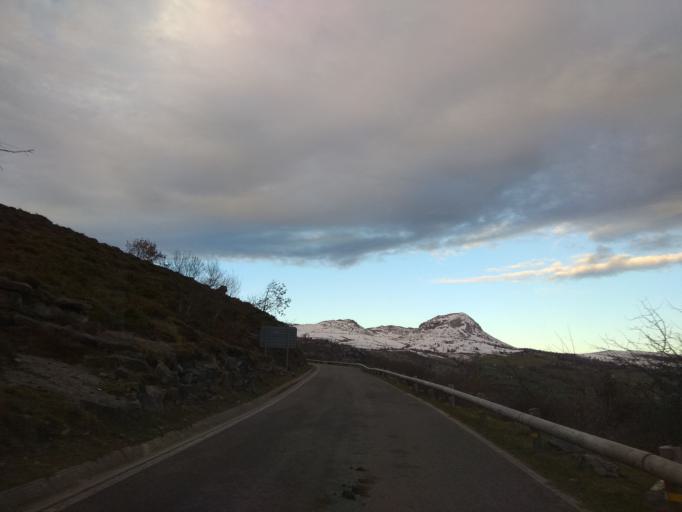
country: ES
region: Cantabria
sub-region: Provincia de Cantabria
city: Arredondo
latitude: 43.1963
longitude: -3.5834
